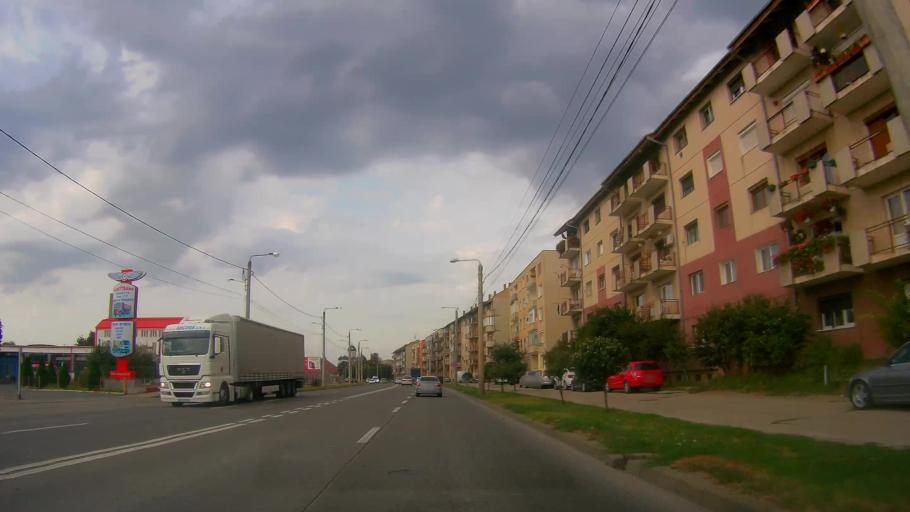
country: RO
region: Satu Mare
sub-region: Municipiul Satu Mare
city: Satu Mare
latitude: 47.7966
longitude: 22.8968
